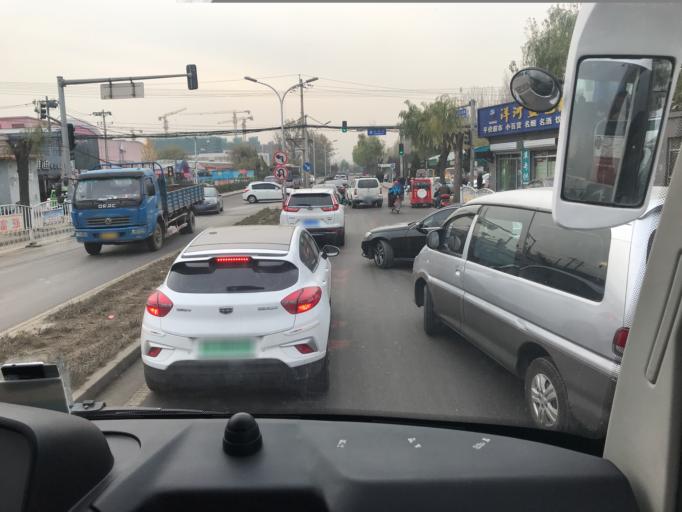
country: CN
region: Beijing
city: Sujiatuo
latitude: 40.0983
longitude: 116.2077
